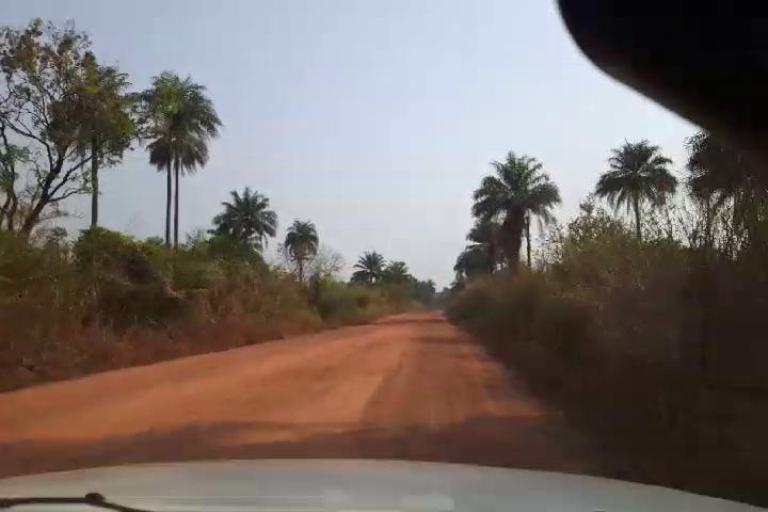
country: SL
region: Northern Province
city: Masingbi
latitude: 8.8140
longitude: -11.8606
